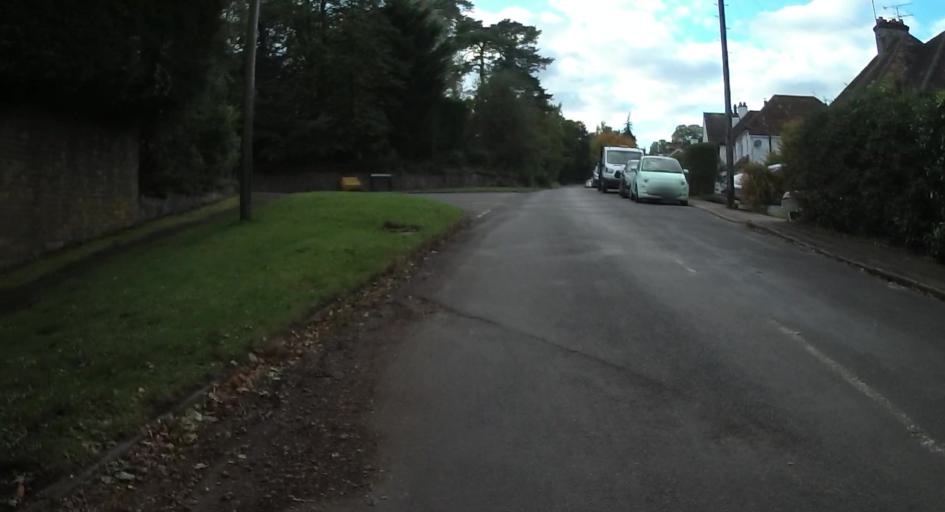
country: GB
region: England
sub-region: Surrey
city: Farnham
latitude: 51.1954
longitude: -0.8056
